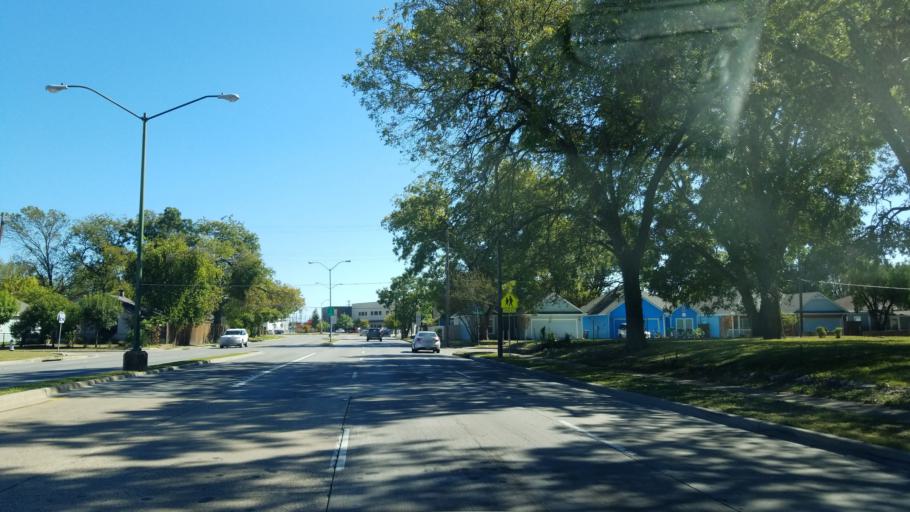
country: US
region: Texas
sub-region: Dallas County
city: Dallas
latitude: 32.7905
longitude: -96.7556
